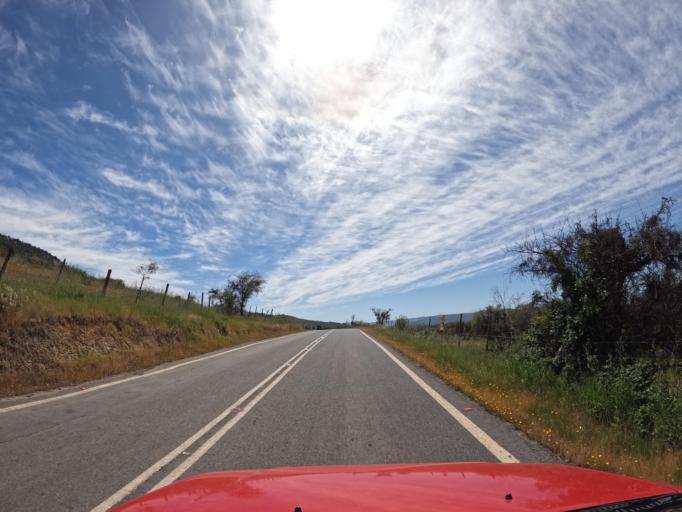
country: CL
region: Maule
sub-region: Provincia de Talca
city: Talca
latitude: -35.0615
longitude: -71.7362
